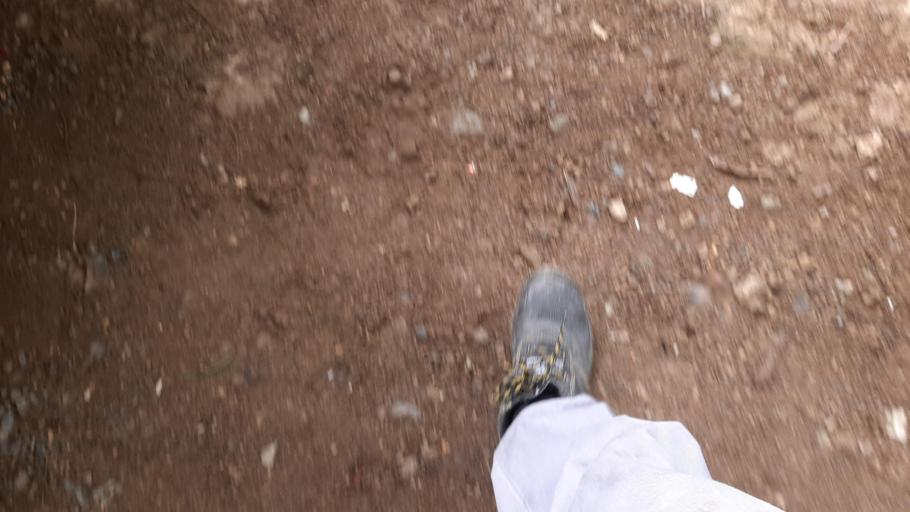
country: PH
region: Central Visayas
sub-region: Province of Cebu
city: Tajao
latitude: 10.3286
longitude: 123.6099
